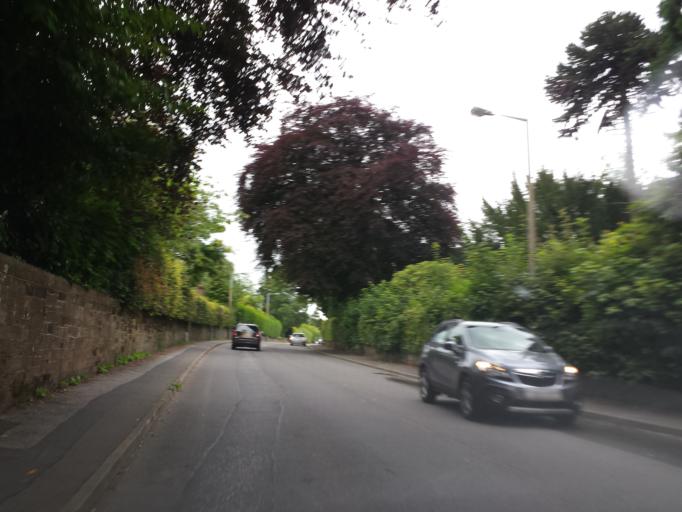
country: GB
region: Scotland
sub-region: Dumfries and Galloway
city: Dumfries
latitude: 55.0604
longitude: -3.6021
